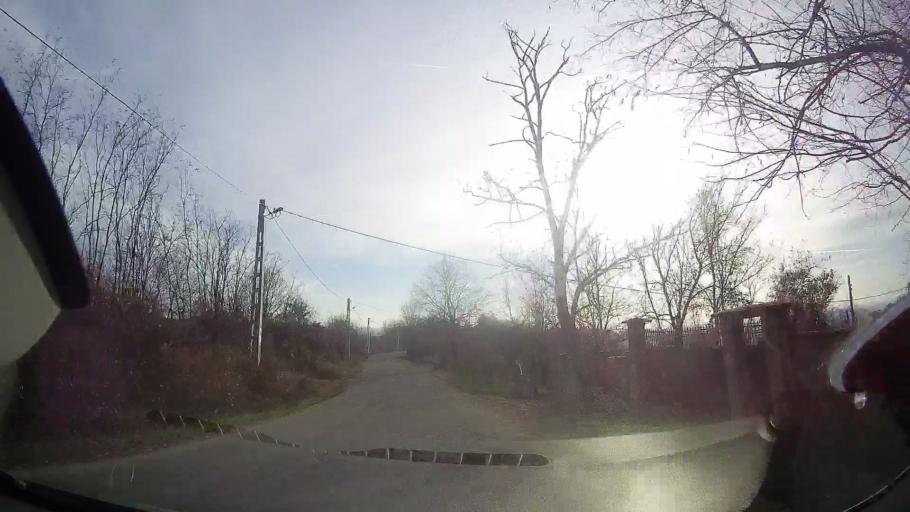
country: RO
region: Bihor
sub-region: Comuna Sarbi
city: Burzuc
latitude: 47.1154
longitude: 22.1793
